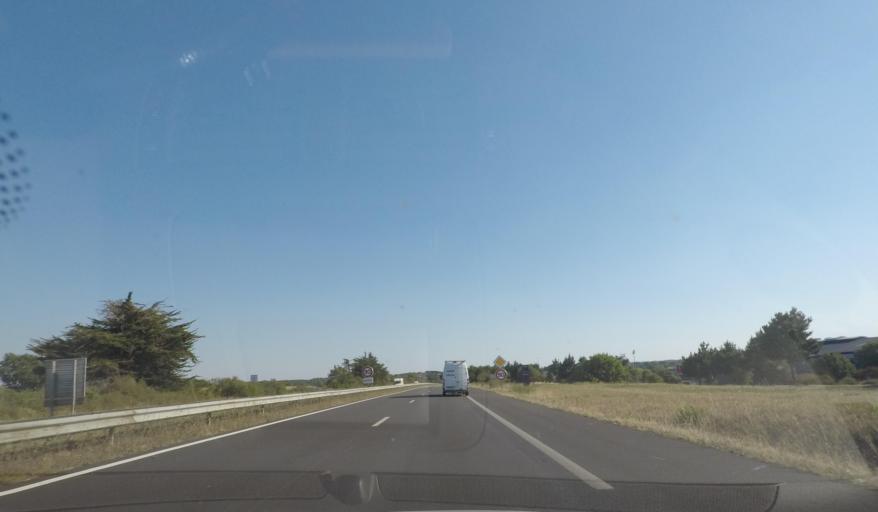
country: FR
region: Pays de la Loire
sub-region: Departement de la Loire-Atlantique
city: Saint-Michel-Chef-Chef
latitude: 47.1720
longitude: -2.1443
